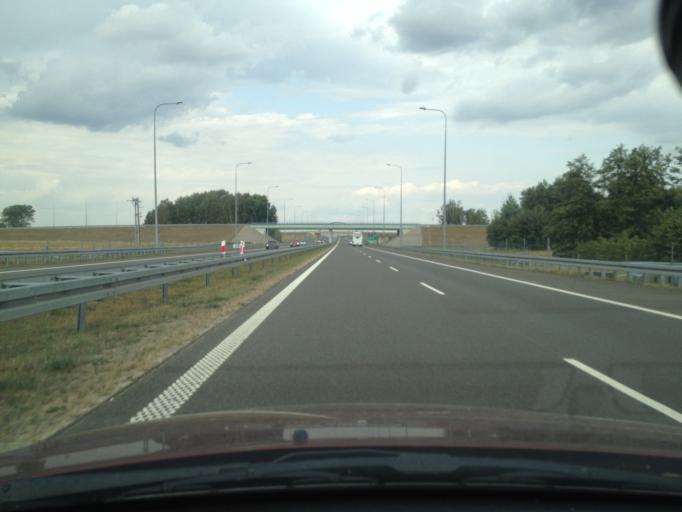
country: PL
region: West Pomeranian Voivodeship
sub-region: Powiat pyrzycki
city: Kozielice
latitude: 53.1172
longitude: 14.7468
